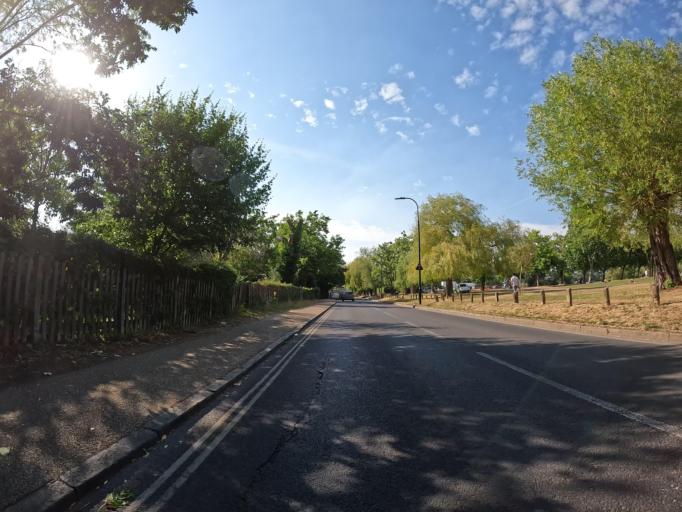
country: GB
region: England
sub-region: Greater London
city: Hadley Wood
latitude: 51.6706
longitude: -0.1628
